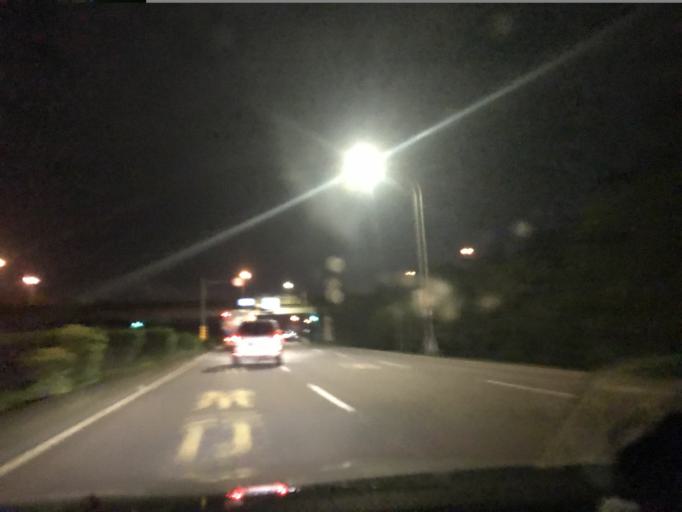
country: TW
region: Taiwan
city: Daxi
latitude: 24.8913
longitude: 121.2657
